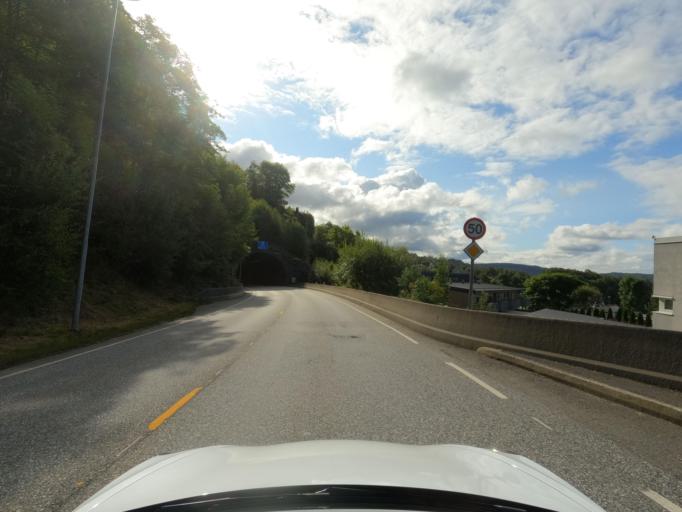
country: NO
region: Hordaland
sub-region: Bergen
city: Bergen
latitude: 60.3400
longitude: 5.3677
